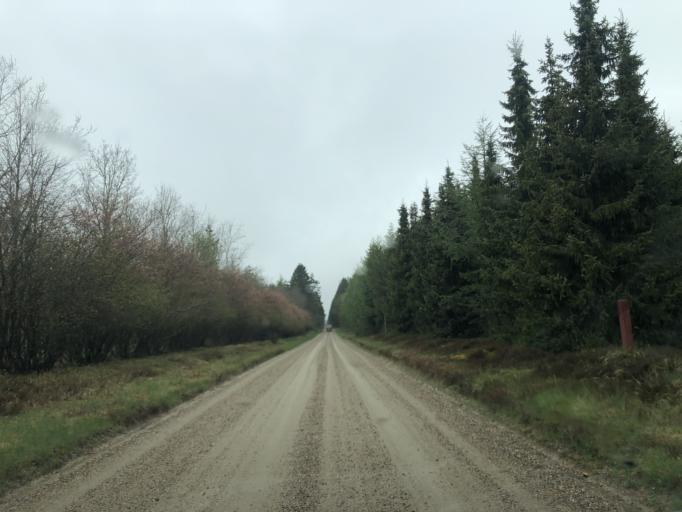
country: DK
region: Central Jutland
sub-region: Lemvig Kommune
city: Lemvig
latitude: 56.4626
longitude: 8.3990
